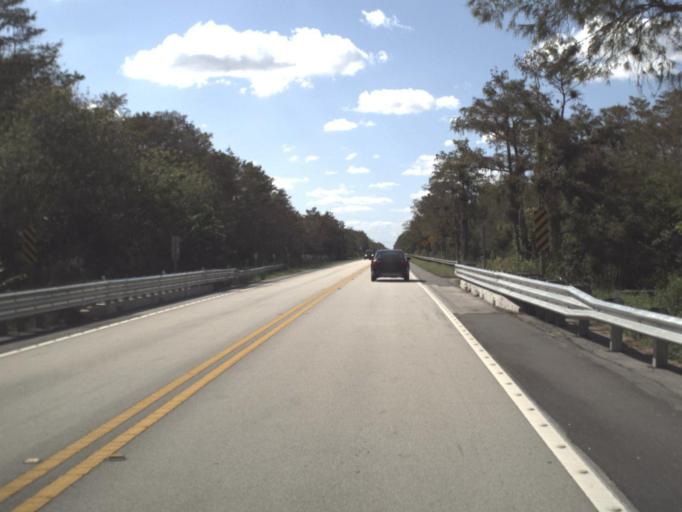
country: US
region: Florida
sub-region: Miami-Dade County
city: Kendall West
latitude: 25.8461
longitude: -80.9266
